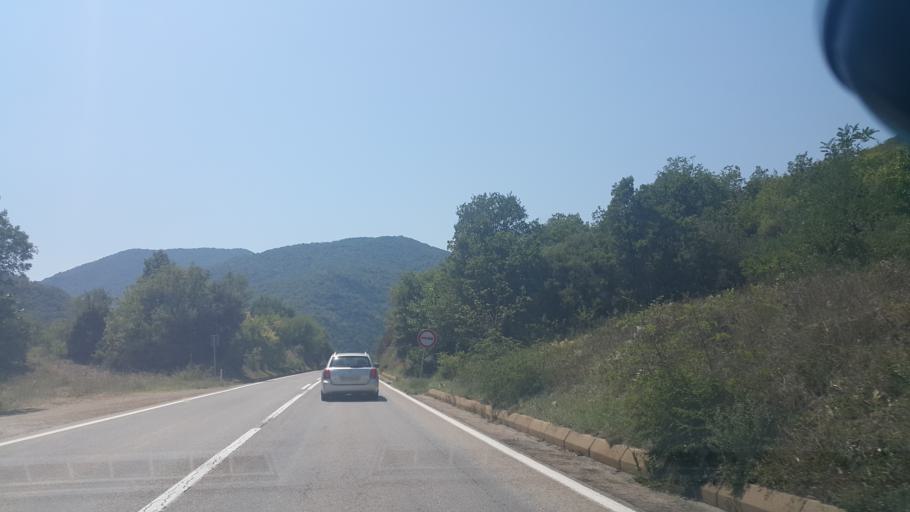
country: MK
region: Gevgelija
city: Miravci
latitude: 41.3780
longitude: 22.3928
